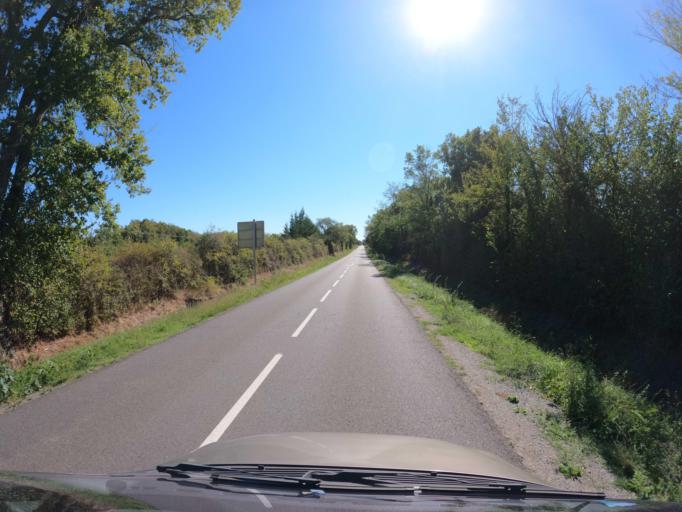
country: FR
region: Poitou-Charentes
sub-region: Departement de la Vienne
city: Saulge
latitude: 46.3801
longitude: 0.9215
